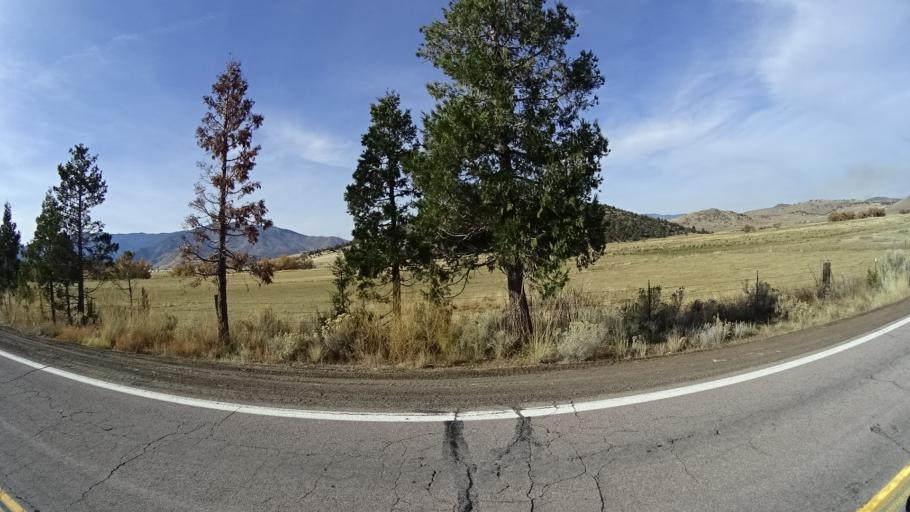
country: US
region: California
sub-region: Siskiyou County
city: Weed
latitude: 41.4799
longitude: -122.4110
